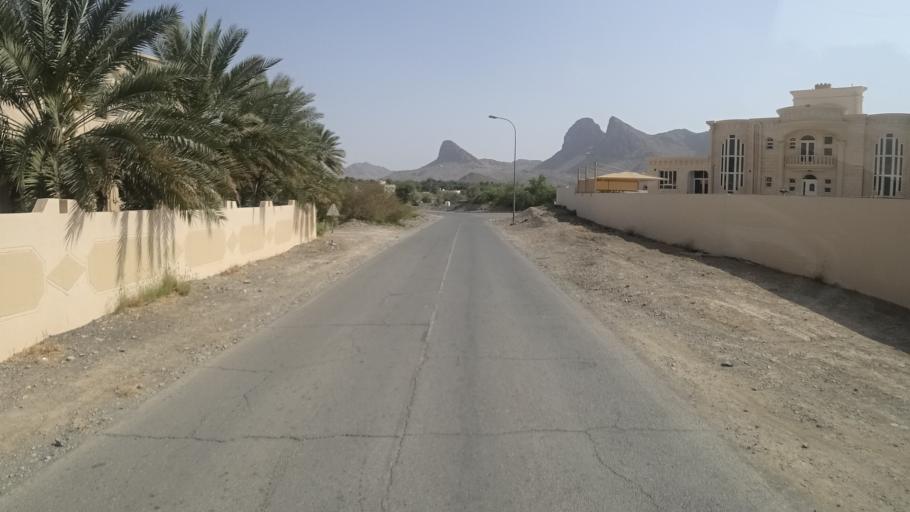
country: OM
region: Muhafazat ad Dakhiliyah
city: Bahla'
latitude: 23.1022
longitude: 57.3021
